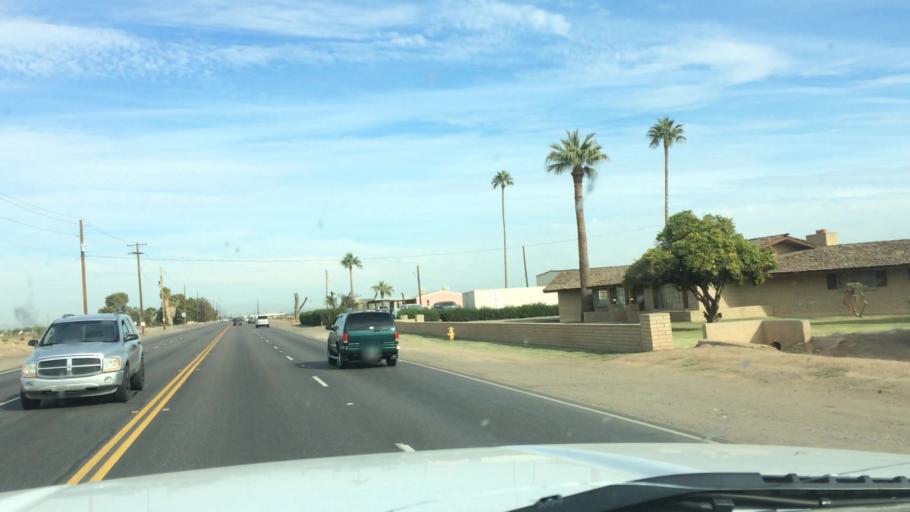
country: US
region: Arizona
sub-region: Maricopa County
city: Tolleson
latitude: 33.4707
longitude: -112.2725
